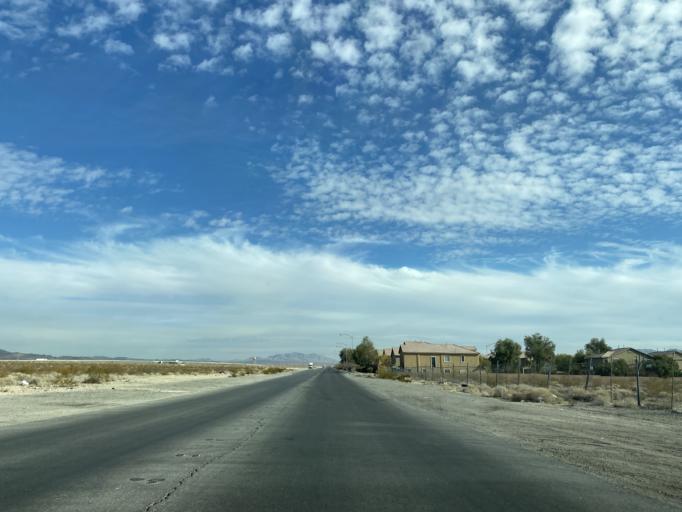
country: US
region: Nevada
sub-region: Clark County
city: Nellis Air Force Base
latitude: 36.2766
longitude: -115.0791
